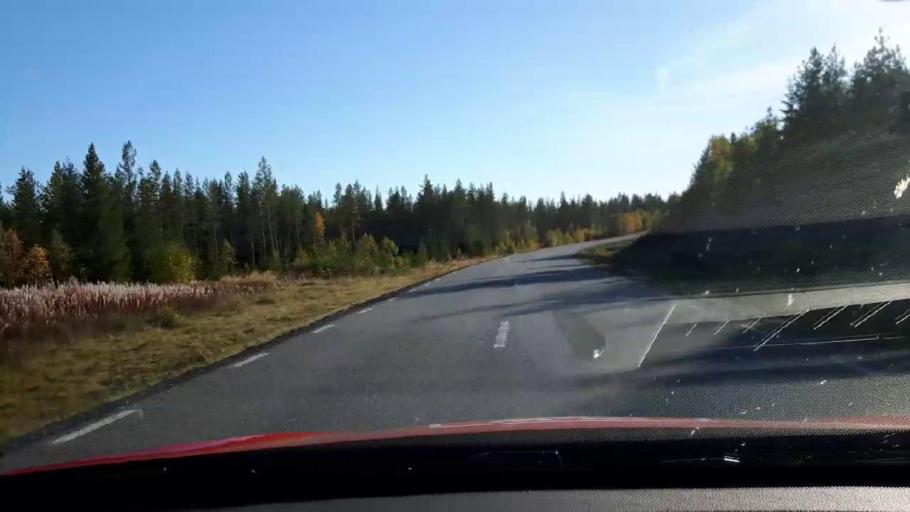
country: SE
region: Jaemtland
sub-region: OEstersunds Kommun
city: Lit
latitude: 63.8419
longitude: 14.9131
